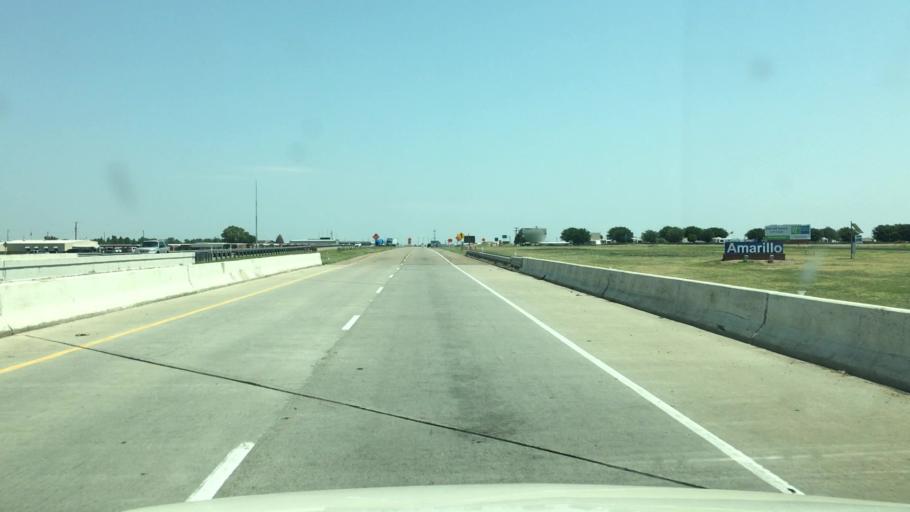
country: US
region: Texas
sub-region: Potter County
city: Bushland
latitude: 35.1872
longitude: -101.9682
